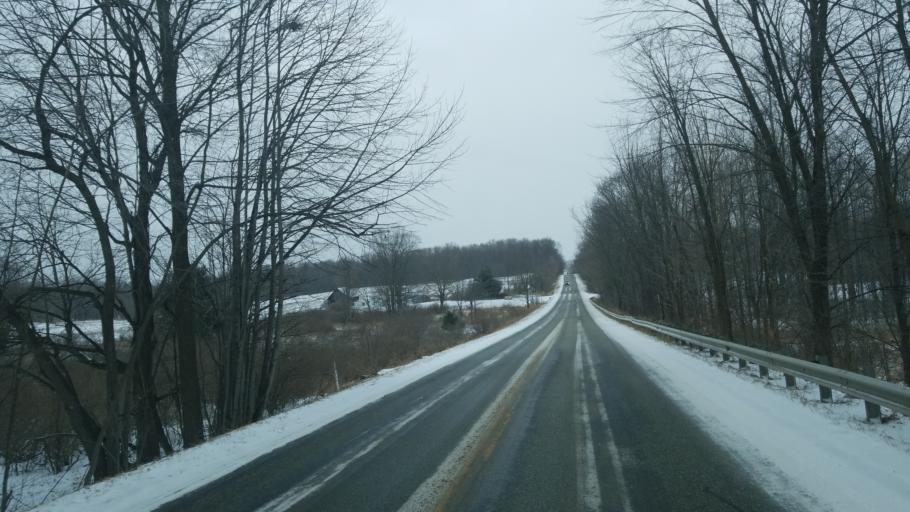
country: US
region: Michigan
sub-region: Osceola County
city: Evart
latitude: 43.9786
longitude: -85.2466
